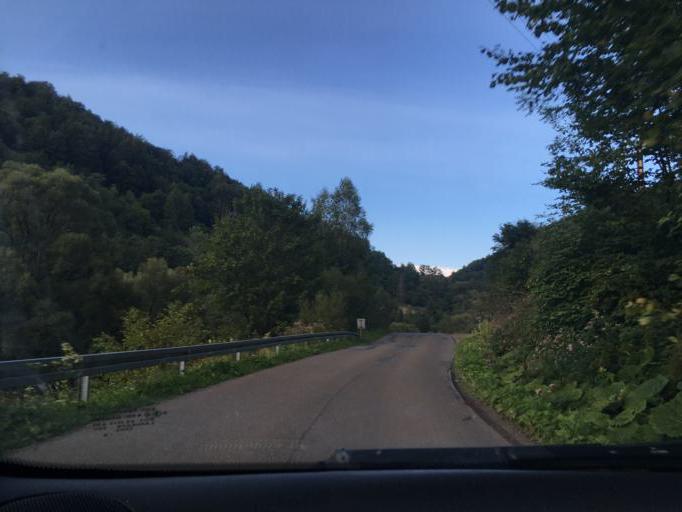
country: PL
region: Subcarpathian Voivodeship
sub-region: Powiat leski
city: Cisna
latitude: 49.2264
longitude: 22.3617
